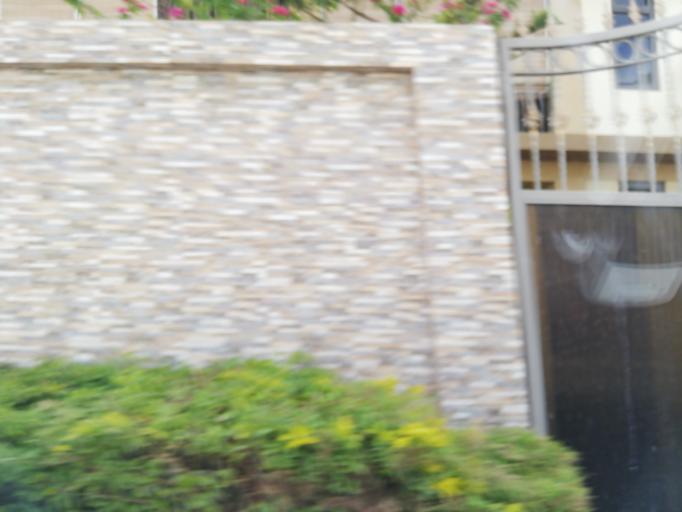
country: MU
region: Plaines Wilhems
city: Ebene
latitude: -20.2313
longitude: 57.4606
